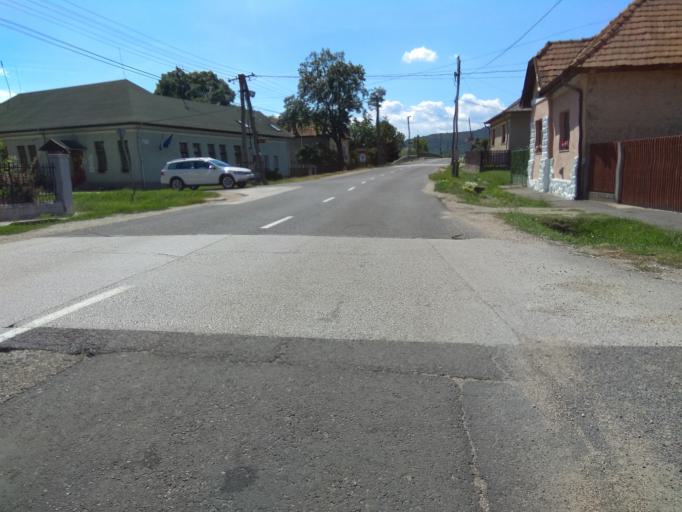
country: HU
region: Borsod-Abauj-Zemplen
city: Sajokaza
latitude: 48.2826
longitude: 20.5825
